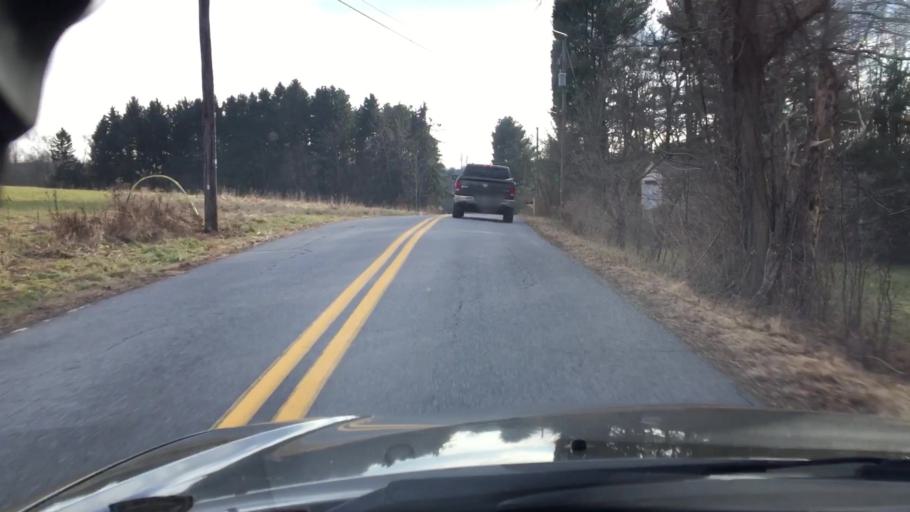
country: US
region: Pennsylvania
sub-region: Luzerne County
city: Back Mountain
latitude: 41.3184
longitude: -76.0666
